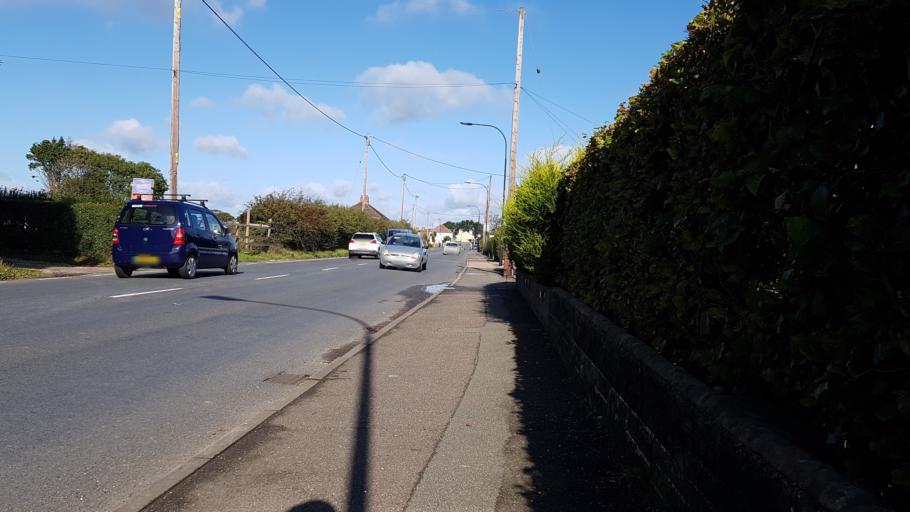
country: GB
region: England
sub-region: Isle of Wight
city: Northwood
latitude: 50.7359
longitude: -1.3068
